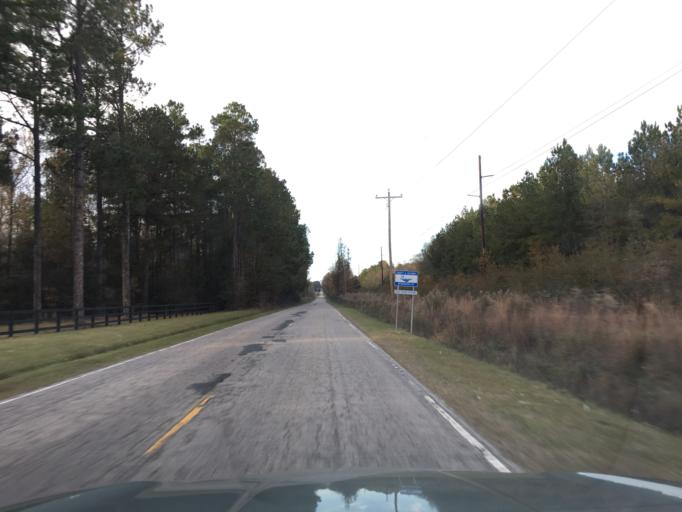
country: US
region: South Carolina
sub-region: Lexington County
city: Red Bank
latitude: 33.7291
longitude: -81.3592
